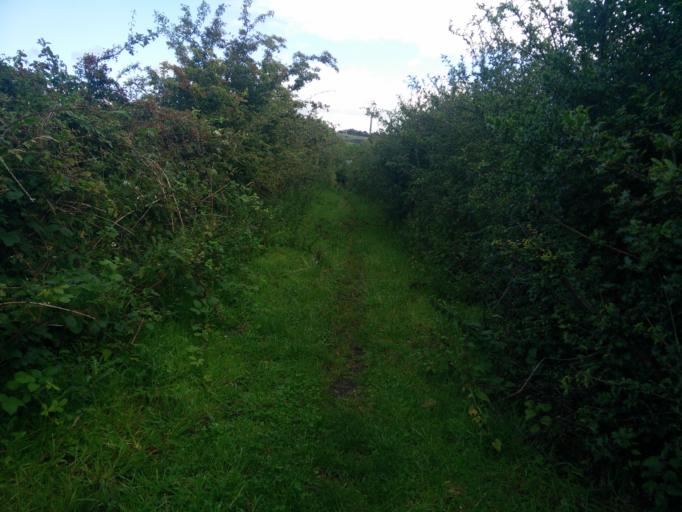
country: GB
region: England
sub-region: County Durham
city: Crook
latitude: 54.7240
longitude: -1.7625
